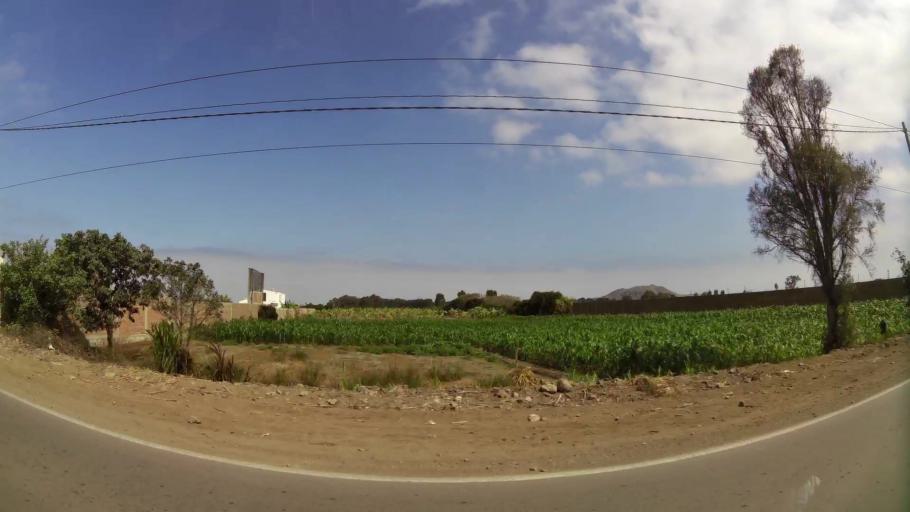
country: PE
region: Lima
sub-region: Provincia de Canete
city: Mala
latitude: -12.7010
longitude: -76.6229
